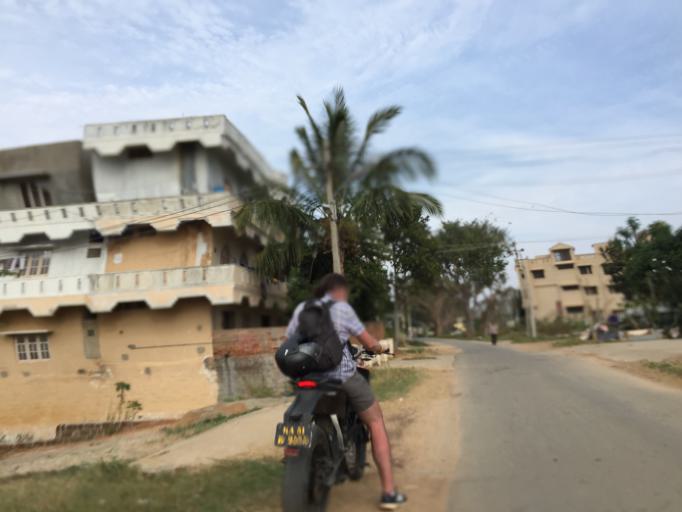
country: IN
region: Karnataka
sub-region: Kolar
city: Kolar
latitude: 13.1378
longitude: 78.1156
